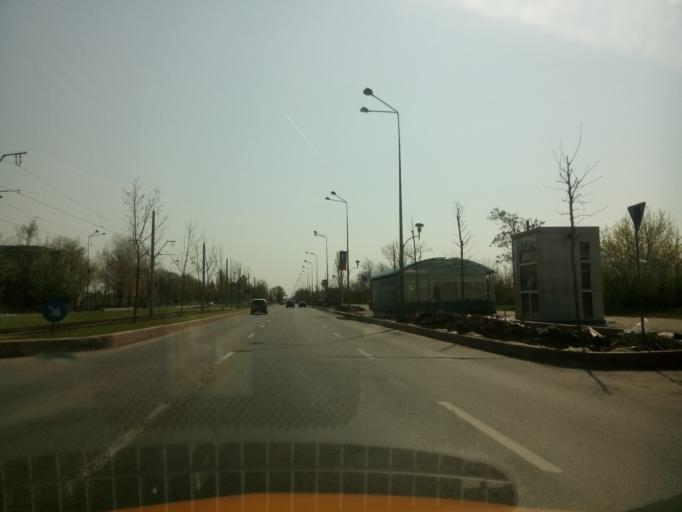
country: RO
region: Ilfov
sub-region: Comuna Glina
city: Catelu
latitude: 44.4075
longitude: 26.1934
